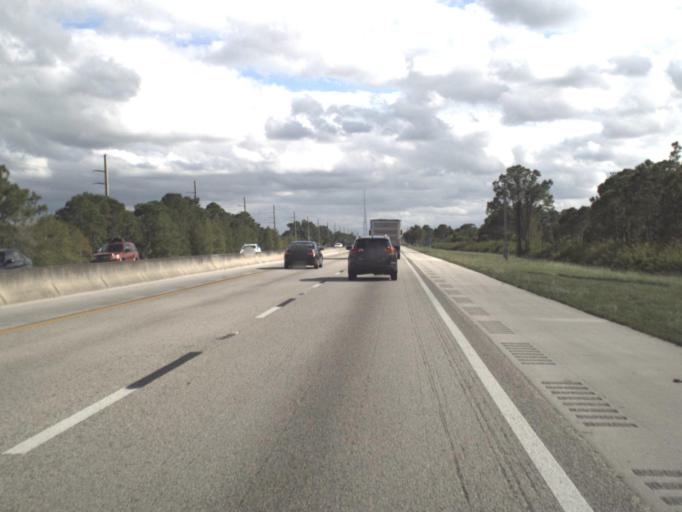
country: US
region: Florida
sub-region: Martin County
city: Palm City
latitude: 27.1801
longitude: -80.3174
